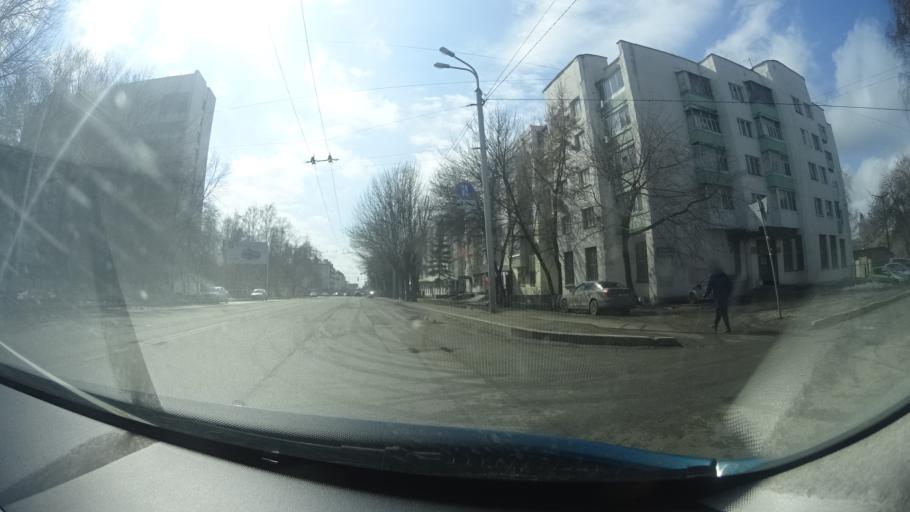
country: RU
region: Bashkortostan
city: Ufa
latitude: 54.7380
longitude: 55.9659
